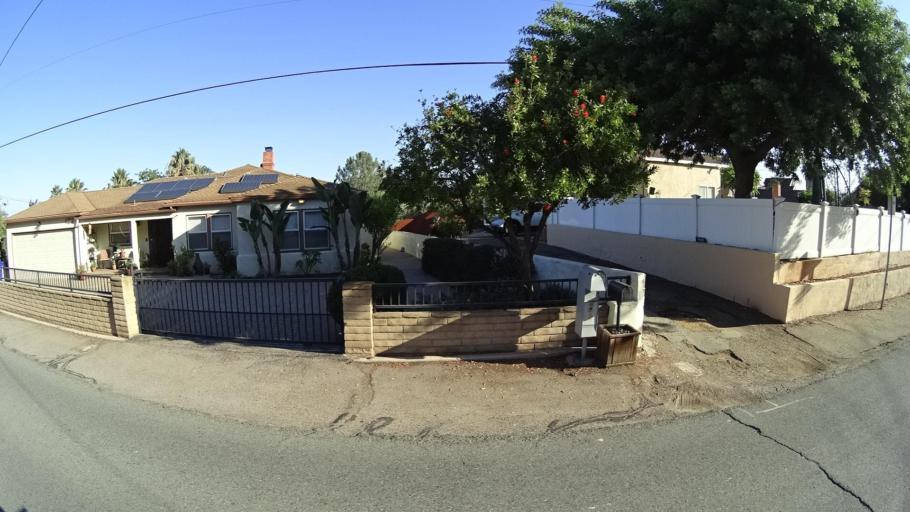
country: US
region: California
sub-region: San Diego County
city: Casa de Oro-Mount Helix
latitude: 32.7781
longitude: -116.9923
